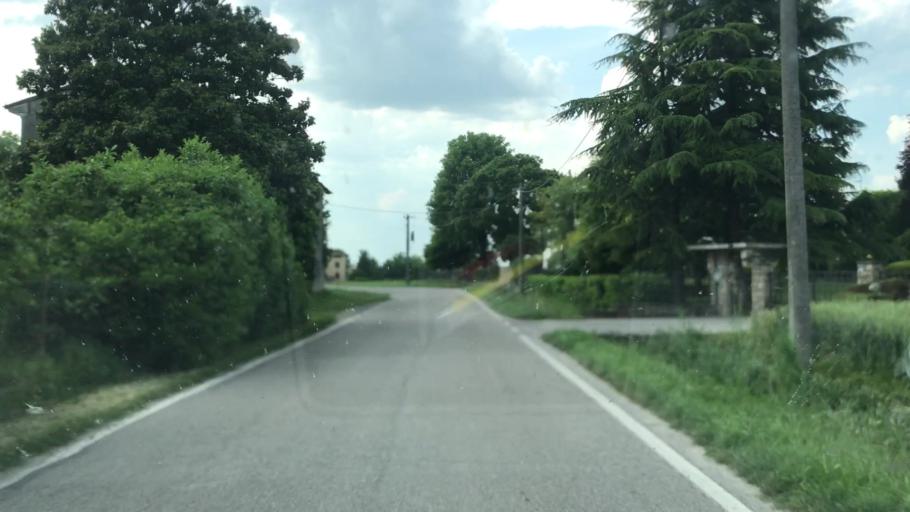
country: IT
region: Lombardy
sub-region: Provincia di Mantova
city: Castel Goffredo
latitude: 45.2928
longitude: 10.5004
